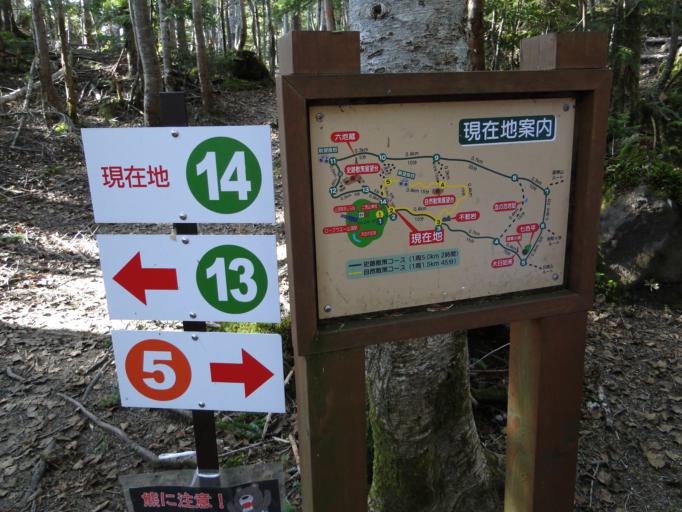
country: JP
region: Tochigi
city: Nikko
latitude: 36.8080
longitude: 139.3559
